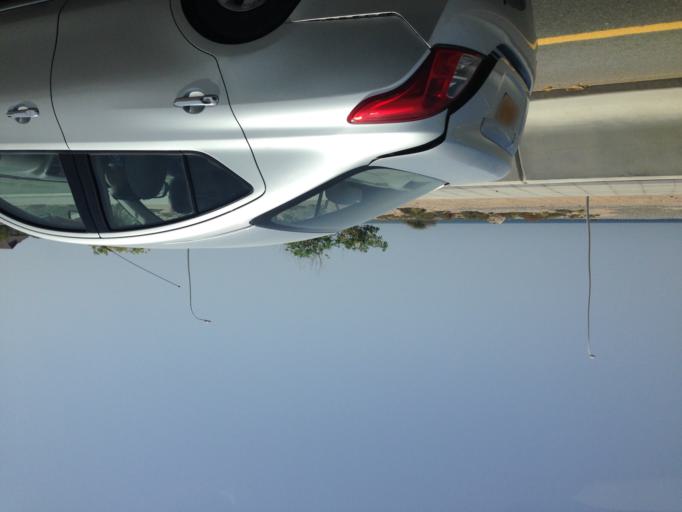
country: OM
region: Muhafazat Masqat
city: Bawshar
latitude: 23.6032
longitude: 58.3390
